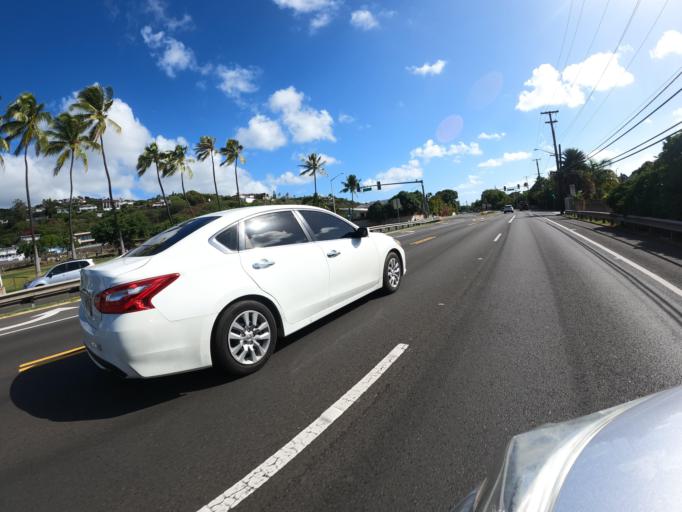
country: US
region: Hawaii
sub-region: Honolulu County
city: Waimanalo
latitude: 21.2757
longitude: -157.7682
